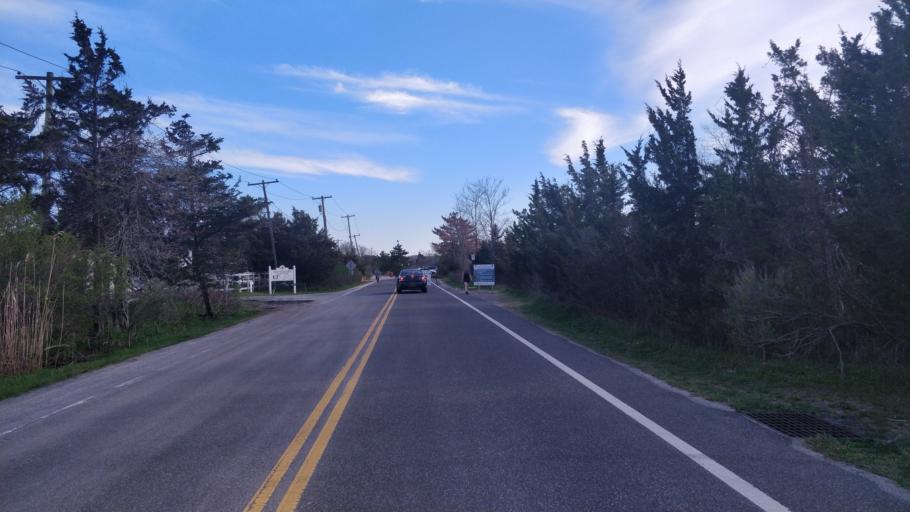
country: US
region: New York
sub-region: Suffolk County
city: Stony Brook
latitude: 40.9444
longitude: -73.1435
